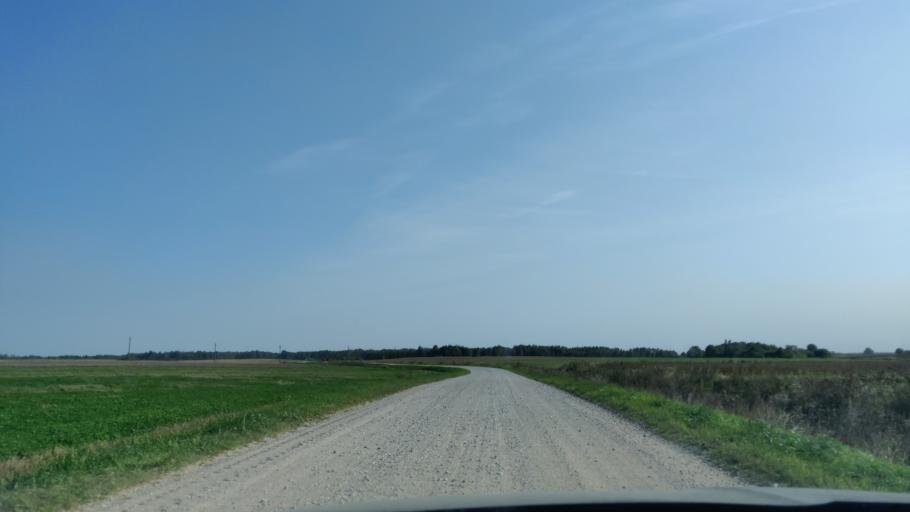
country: LT
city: Sirvintos
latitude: 54.9691
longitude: 24.8418
